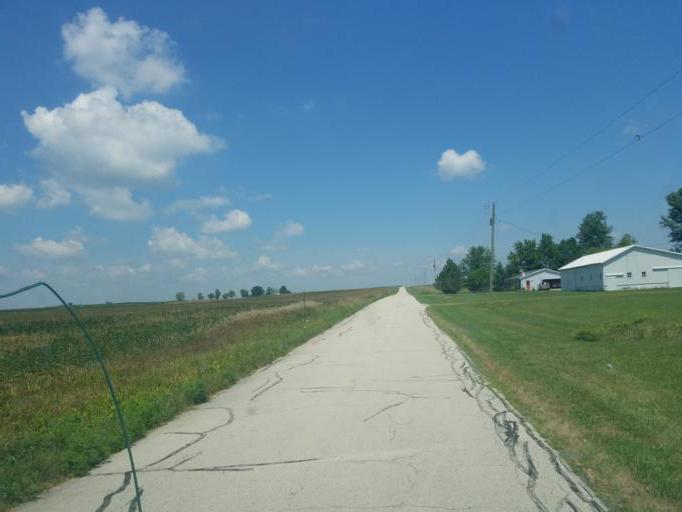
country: US
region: Ohio
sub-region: Allen County
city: Spencerville
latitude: 40.6718
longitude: -84.4350
